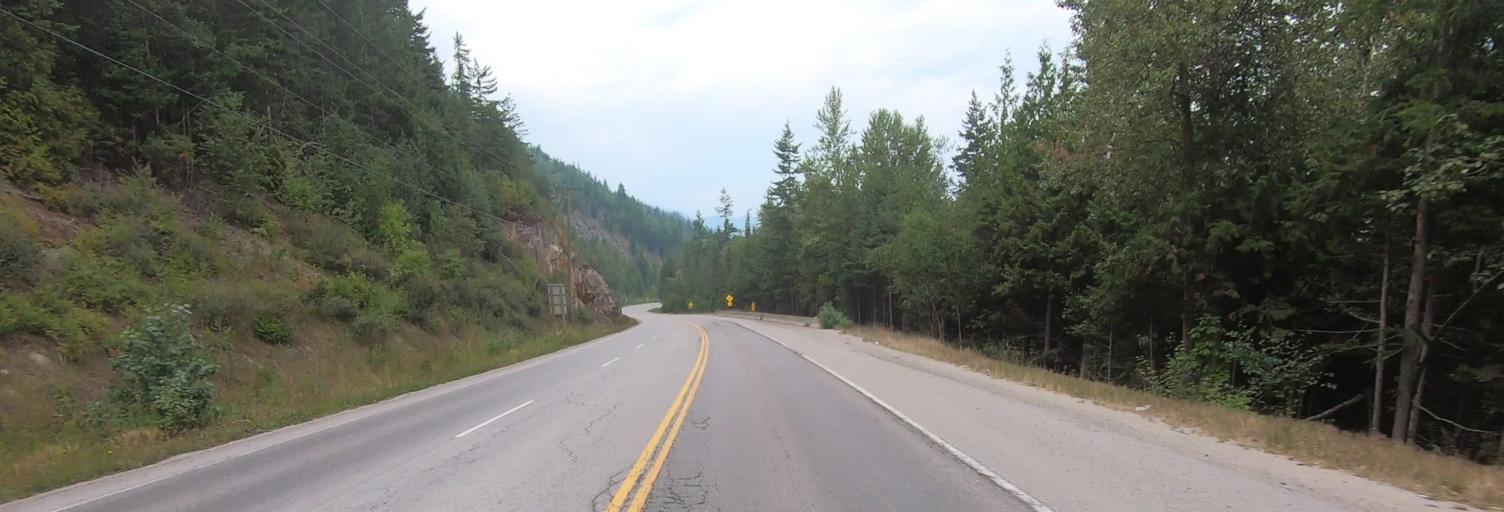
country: CA
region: British Columbia
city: Salmon Arm
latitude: 50.7636
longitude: -119.3339
